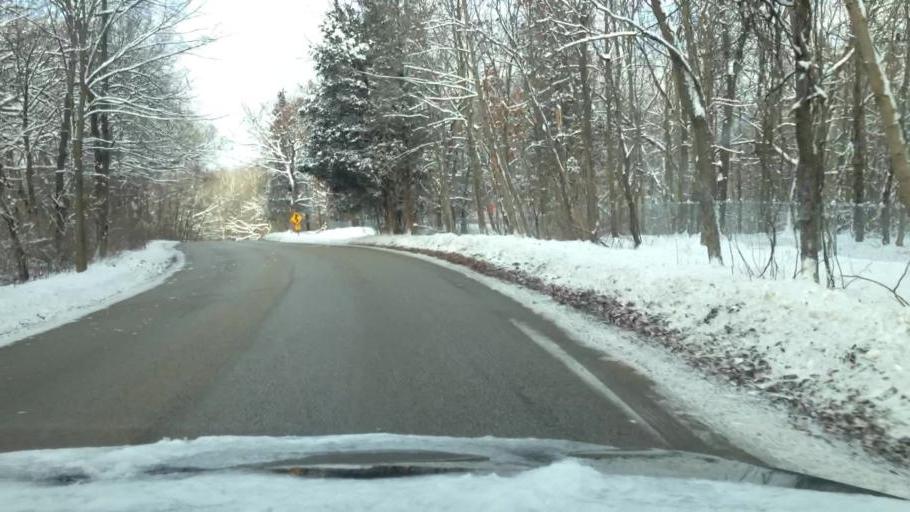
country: US
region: Wisconsin
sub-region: Walworth County
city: East Troy
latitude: 42.8070
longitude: -88.4251
